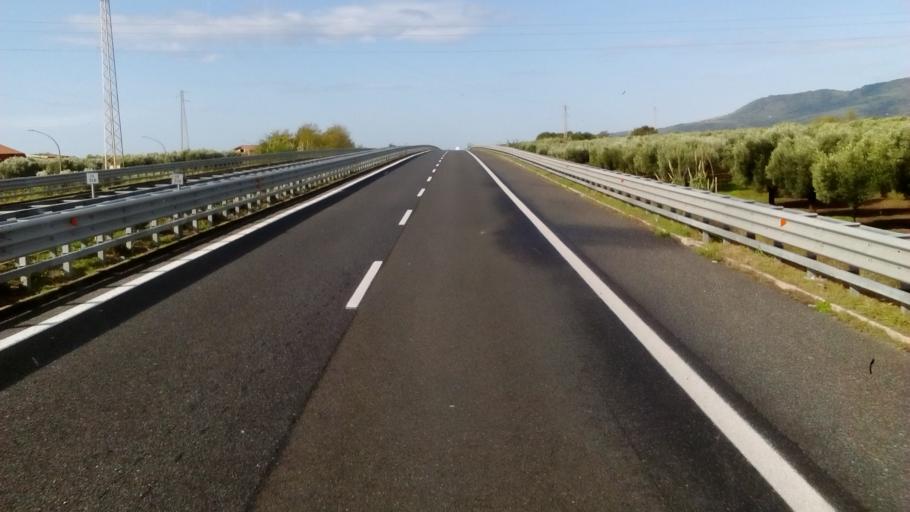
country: IT
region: Calabria
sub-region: Provincia di Catanzaro
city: Santa Eufemia Lamezia
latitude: 38.9253
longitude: 16.2535
